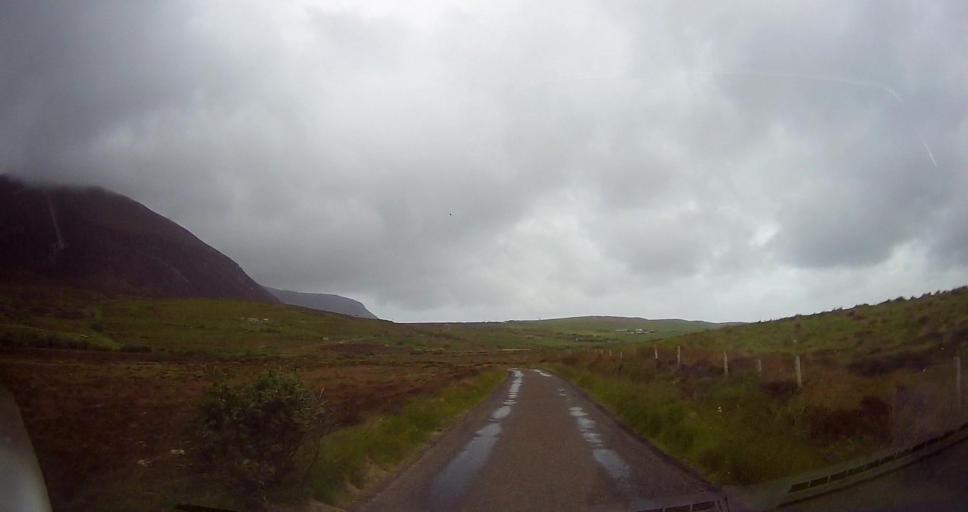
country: GB
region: Scotland
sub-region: Orkney Islands
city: Stromness
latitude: 58.9039
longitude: -3.3078
